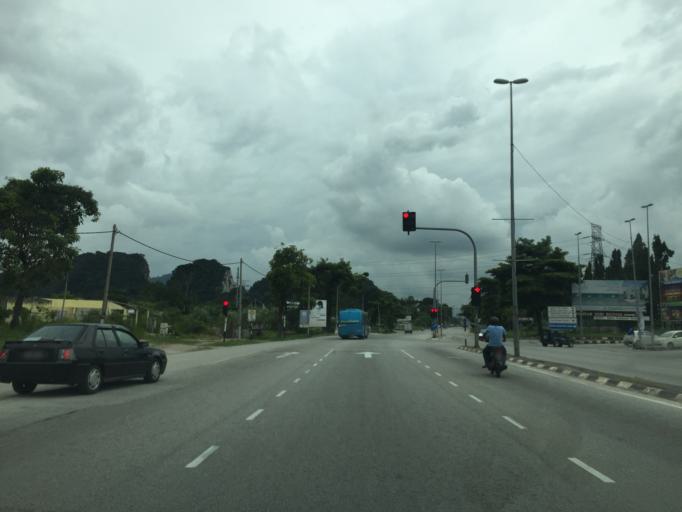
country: MY
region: Perak
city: Ipoh
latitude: 4.5534
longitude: 101.1163
